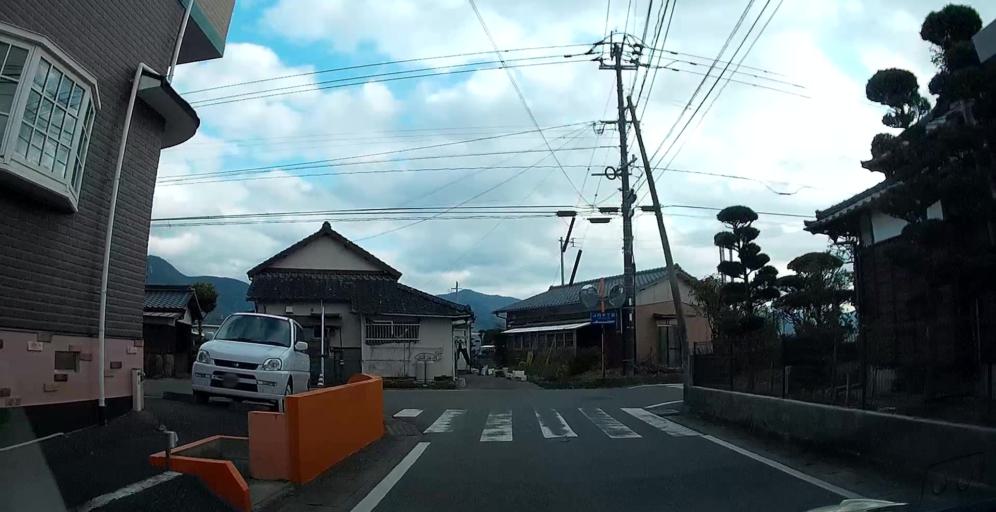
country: JP
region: Kumamoto
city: Yatsushiro
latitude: 32.5310
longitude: 130.6385
